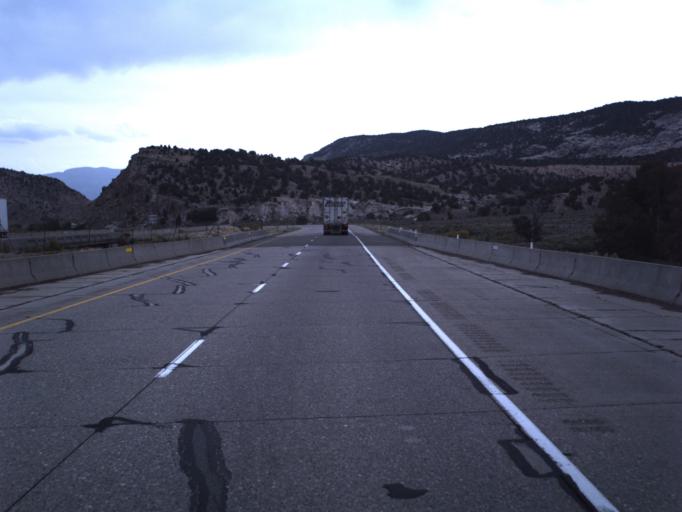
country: US
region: Utah
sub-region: Sevier County
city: Monroe
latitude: 38.5761
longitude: -112.3377
